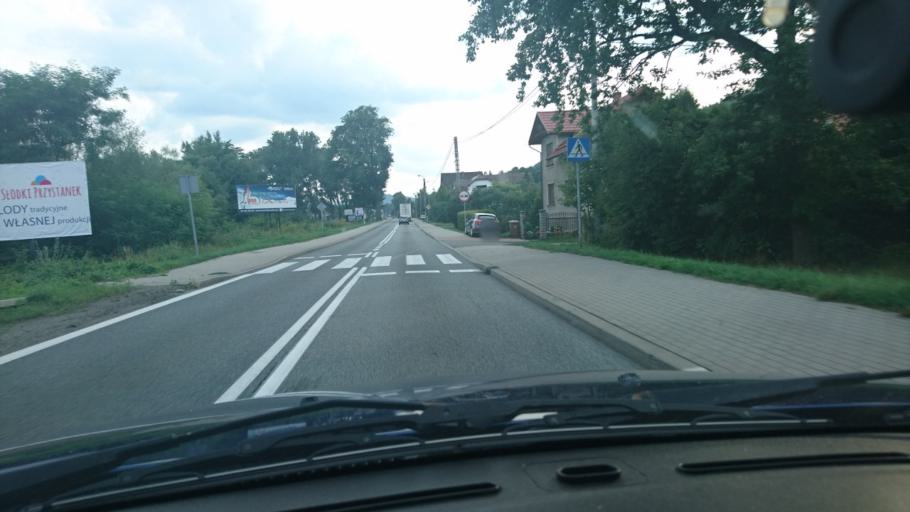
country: PL
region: Silesian Voivodeship
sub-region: Powiat zywiecki
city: Wegierska Gorka
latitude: 49.6183
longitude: 19.1267
